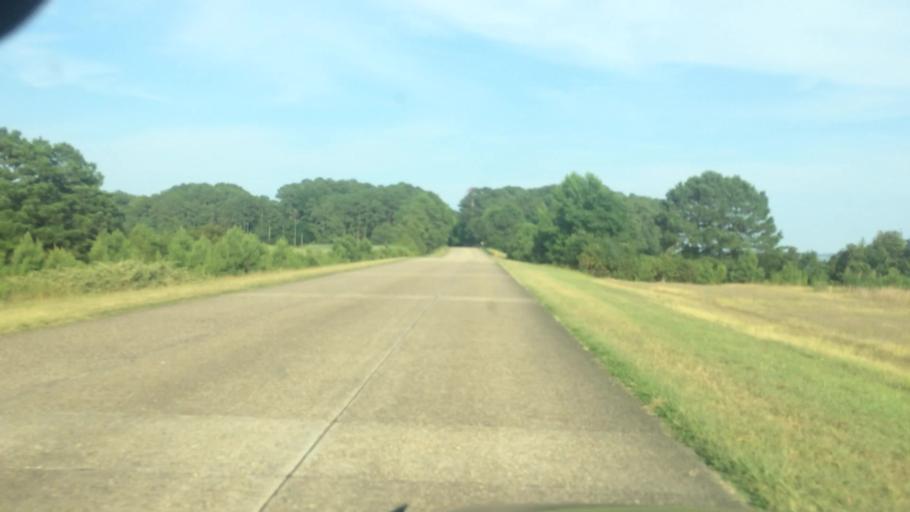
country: US
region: Virginia
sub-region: James City County
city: Williamsburg
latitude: 37.2158
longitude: -76.7471
